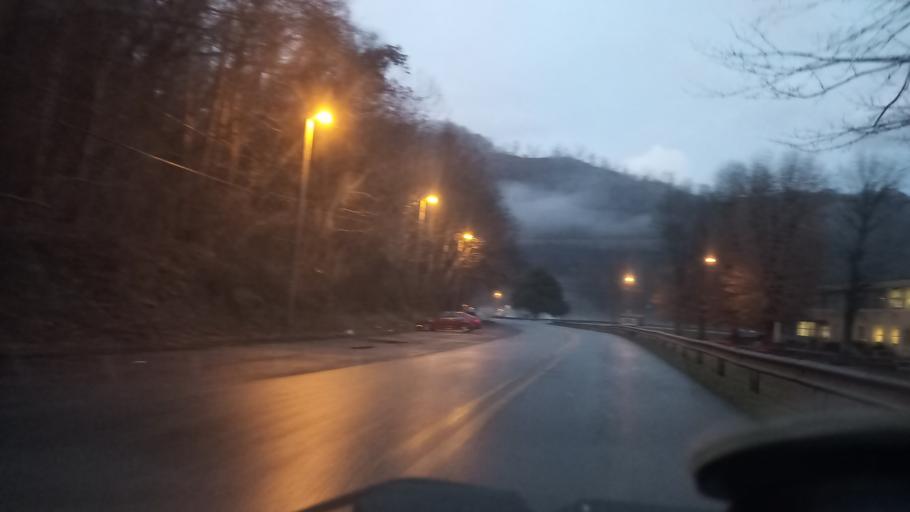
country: US
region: West Virginia
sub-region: Logan County
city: Mallory
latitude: 37.7307
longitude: -81.8777
